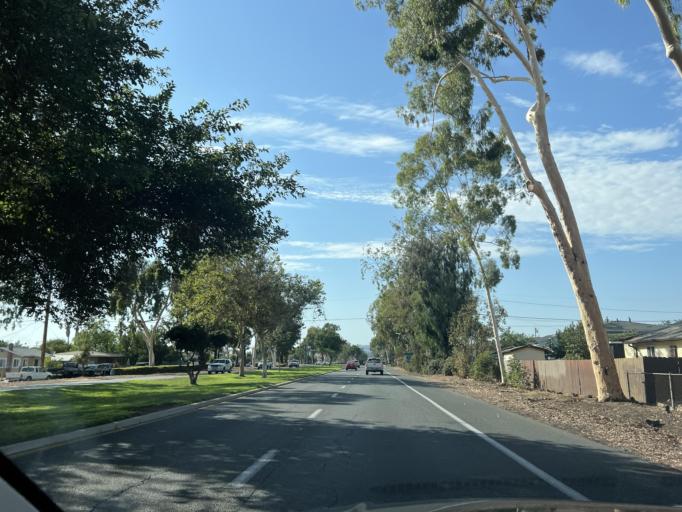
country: US
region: California
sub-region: San Diego County
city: Escondido
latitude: 33.1101
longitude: -117.0802
